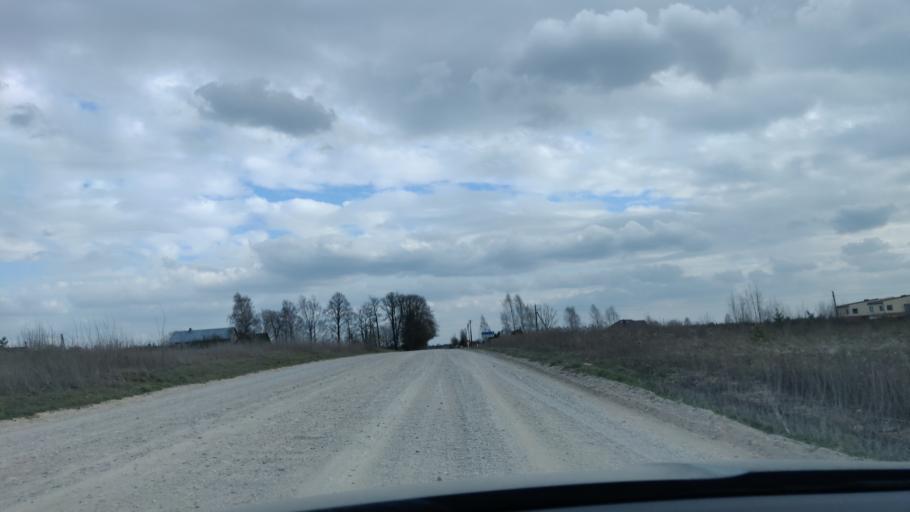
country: LT
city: Lentvaris
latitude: 54.6174
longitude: 25.0673
